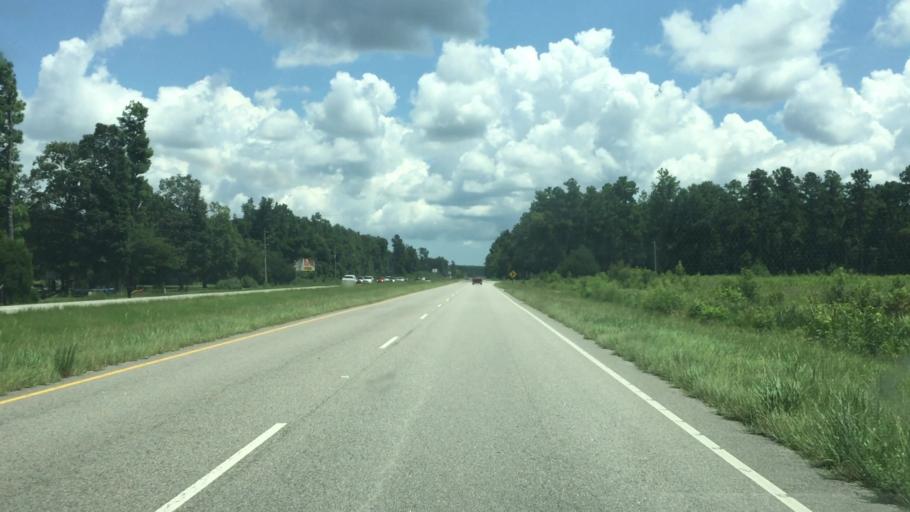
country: US
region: South Carolina
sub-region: Horry County
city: Loris
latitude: 34.0137
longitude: -78.7824
